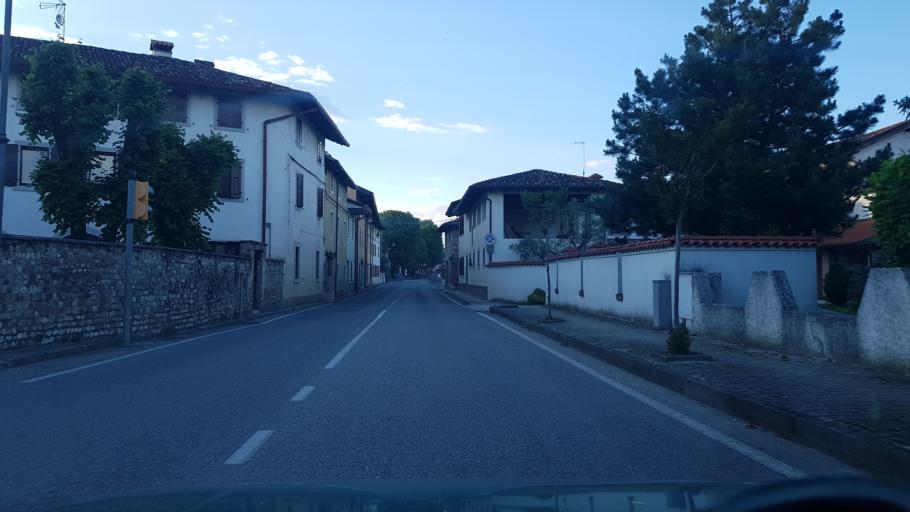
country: IT
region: Friuli Venezia Giulia
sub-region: Provincia di Udine
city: Santa Maria la Longa
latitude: 45.9209
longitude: 13.2946
